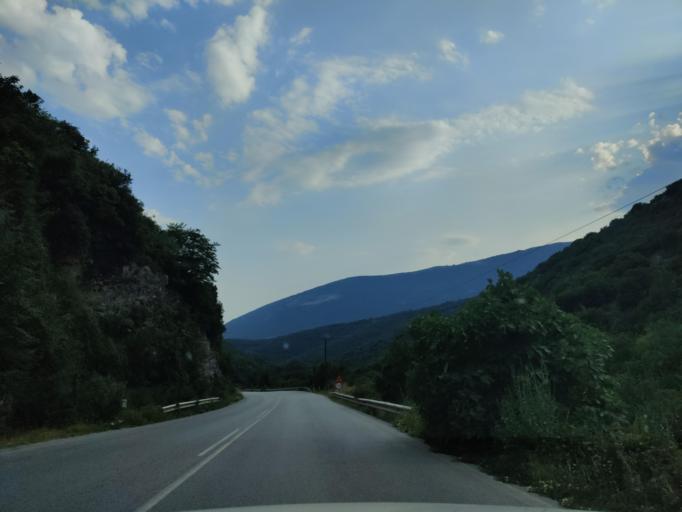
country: GR
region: East Macedonia and Thrace
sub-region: Nomos Dramas
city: Volakas
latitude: 41.2714
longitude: 23.9755
